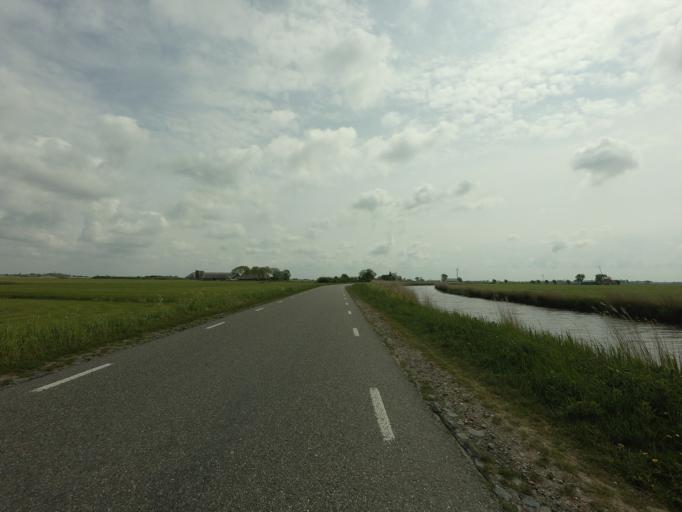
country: NL
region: Friesland
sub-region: Sudwest Fryslan
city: Bolsward
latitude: 53.1052
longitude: 5.5103
